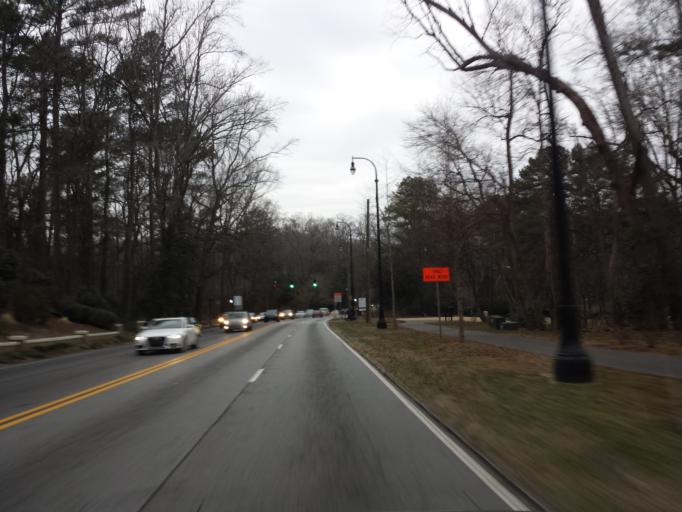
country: US
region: Georgia
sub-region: DeKalb County
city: Druid Hills
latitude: 33.7717
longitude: -84.3239
